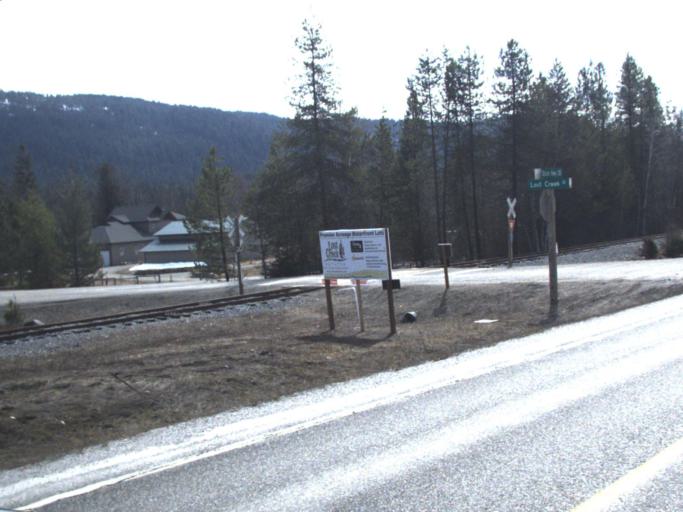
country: US
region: Washington
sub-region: Stevens County
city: Chewelah
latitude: 48.6297
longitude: -117.3688
